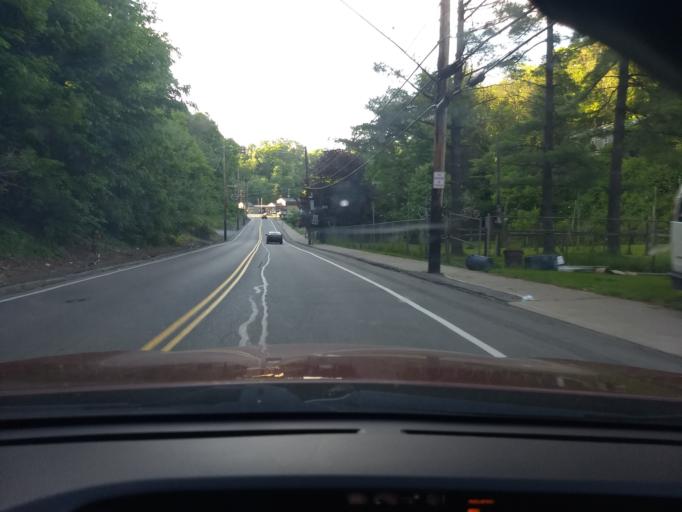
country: US
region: Pennsylvania
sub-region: Allegheny County
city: White Oak
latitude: 40.3526
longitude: -79.8339
